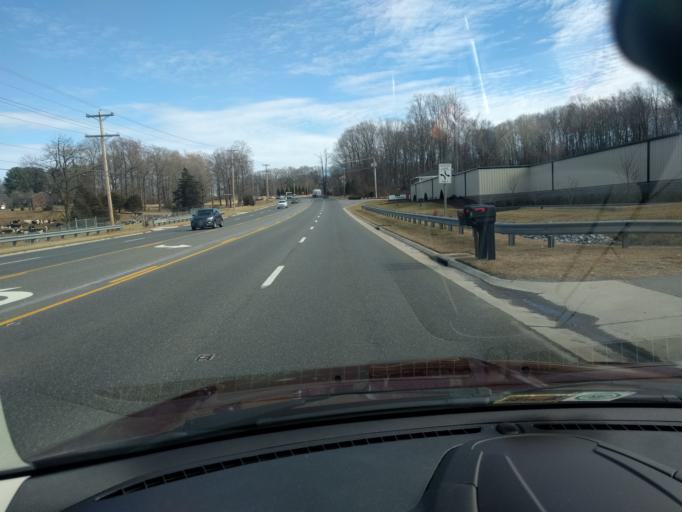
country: US
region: Virginia
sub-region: Bedford County
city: Forest
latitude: 37.3651
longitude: -79.2731
